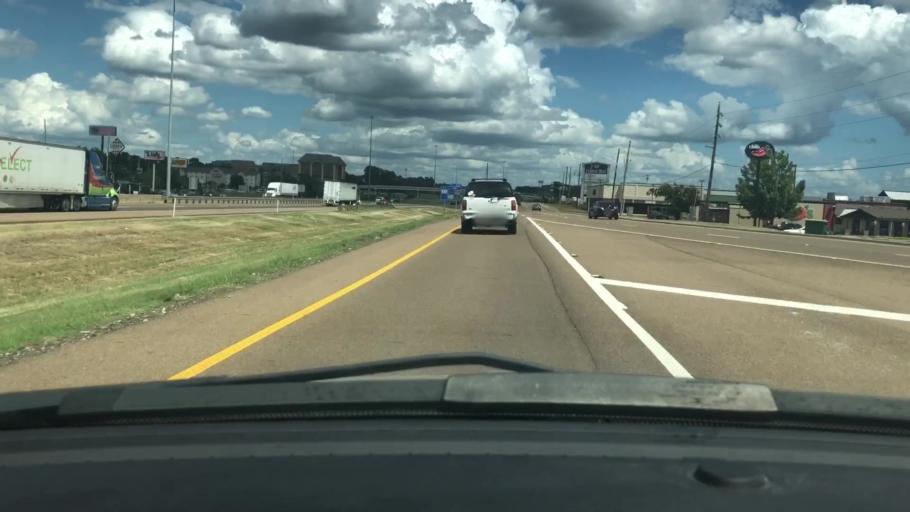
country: US
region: Texas
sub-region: Bowie County
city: Wake Village
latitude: 33.4575
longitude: -94.0835
